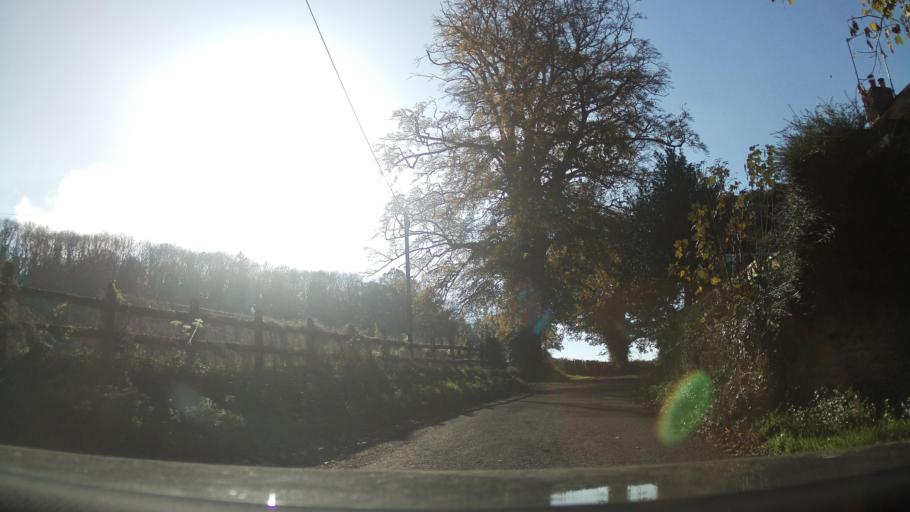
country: GB
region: England
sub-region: Somerset
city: Castle Cary
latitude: 51.0588
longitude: -2.4792
